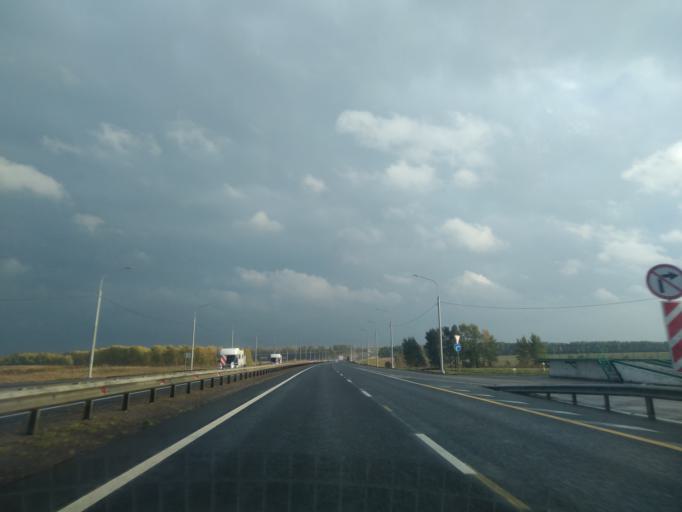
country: RU
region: Lipetsk
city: Yelets
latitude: 52.5731
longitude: 38.6999
